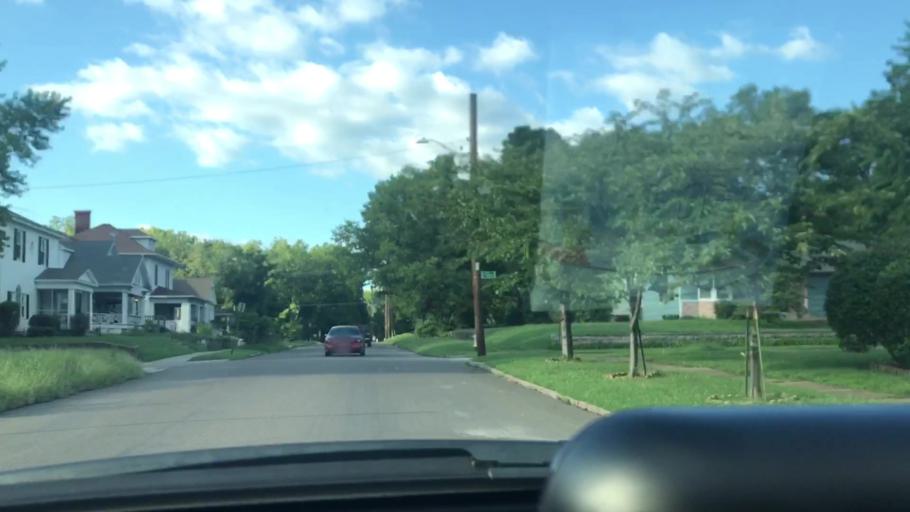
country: US
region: Missouri
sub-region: Pettis County
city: Sedalia
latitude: 38.7025
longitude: -93.2366
